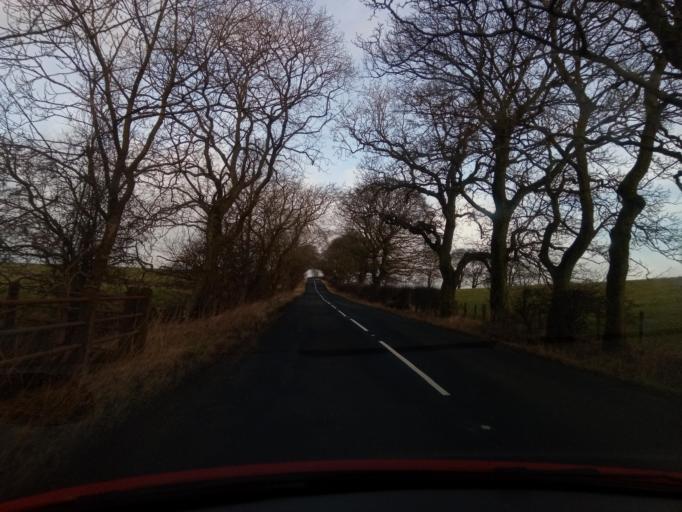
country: GB
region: England
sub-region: Northumberland
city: Acomb
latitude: 55.0869
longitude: -2.0633
